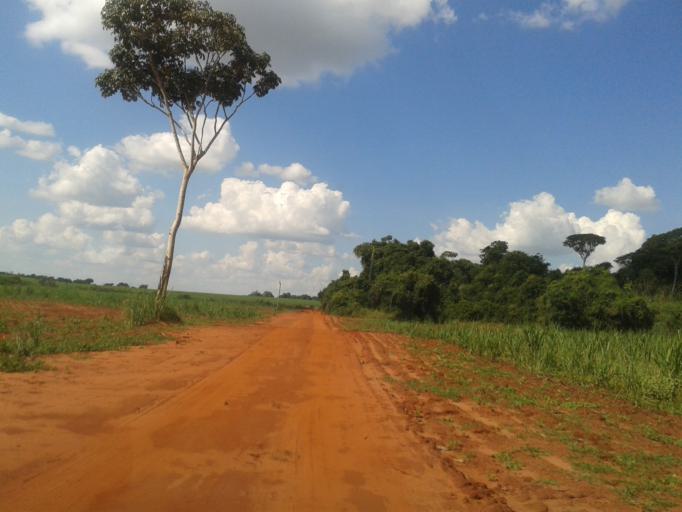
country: BR
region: Minas Gerais
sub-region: Ituiutaba
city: Ituiutaba
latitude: -19.1801
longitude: -49.7215
